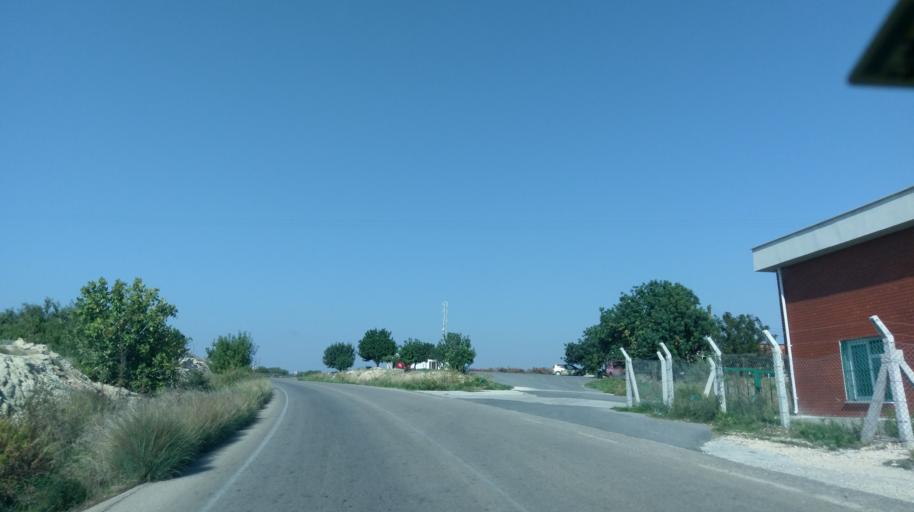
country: CY
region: Ammochostos
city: Leonarisso
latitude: 35.4294
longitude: 34.1281
